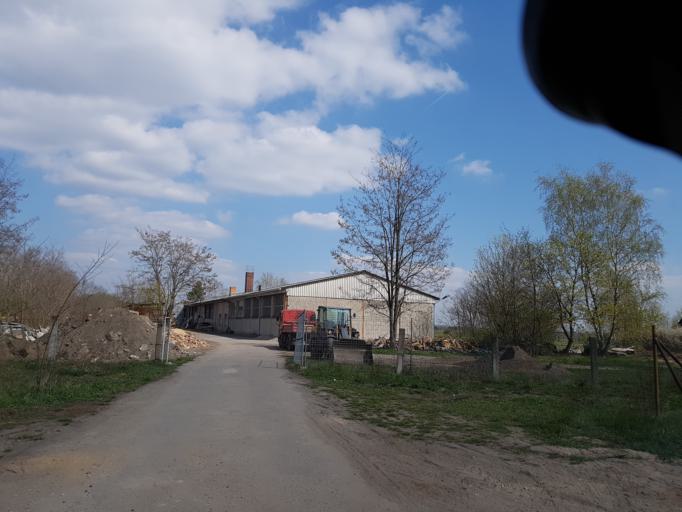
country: DE
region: Brandenburg
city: Bruck
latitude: 52.1869
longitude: 12.7593
